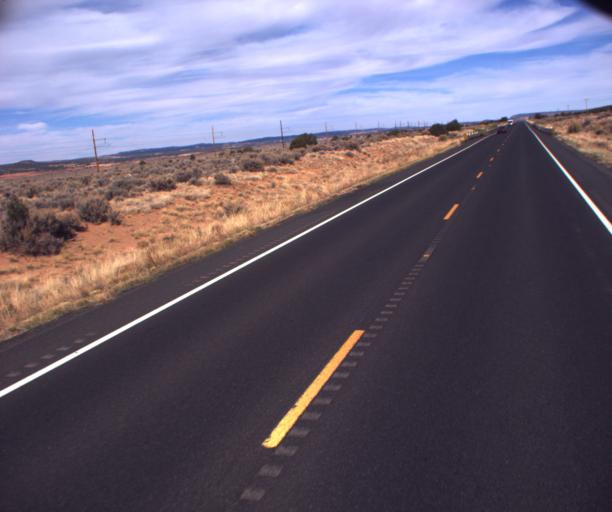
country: US
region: Arizona
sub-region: Navajo County
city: Kayenta
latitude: 36.5066
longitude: -110.6088
